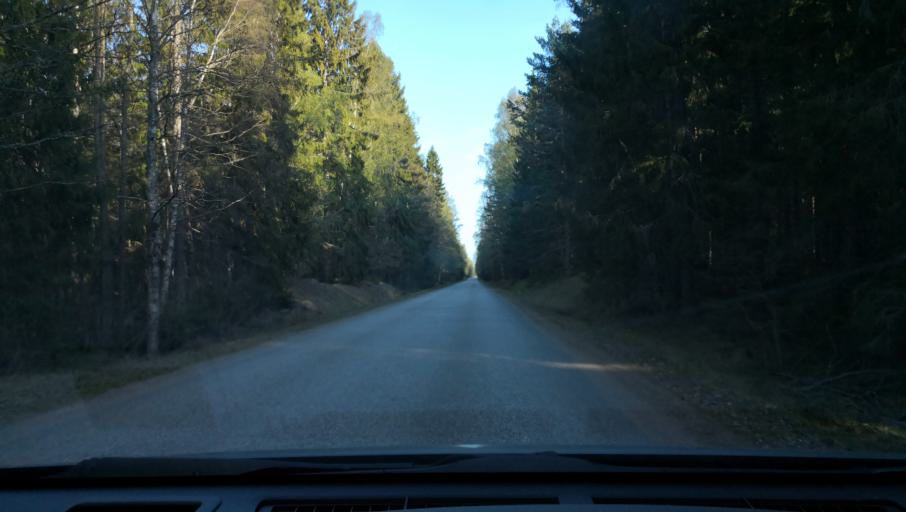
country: SE
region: Uppsala
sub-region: Heby Kommun
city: Tarnsjo
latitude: 60.2778
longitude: 16.8932
